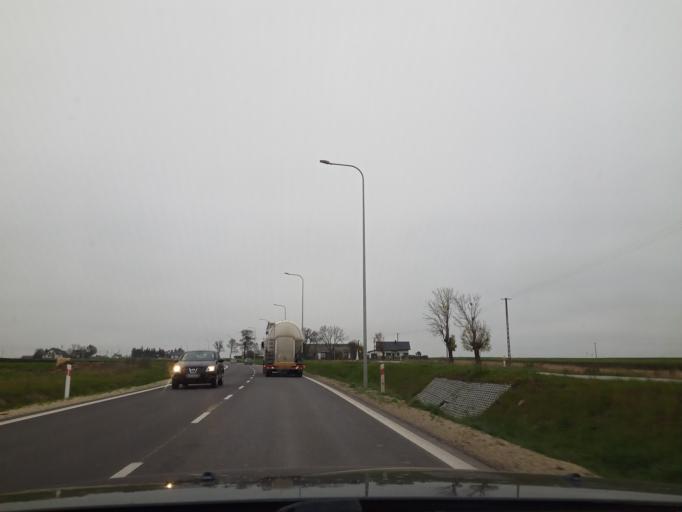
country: PL
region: Swietokrzyskie
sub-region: Powiat jedrzejowski
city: Jedrzejow
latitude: 50.5920
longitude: 20.3221
